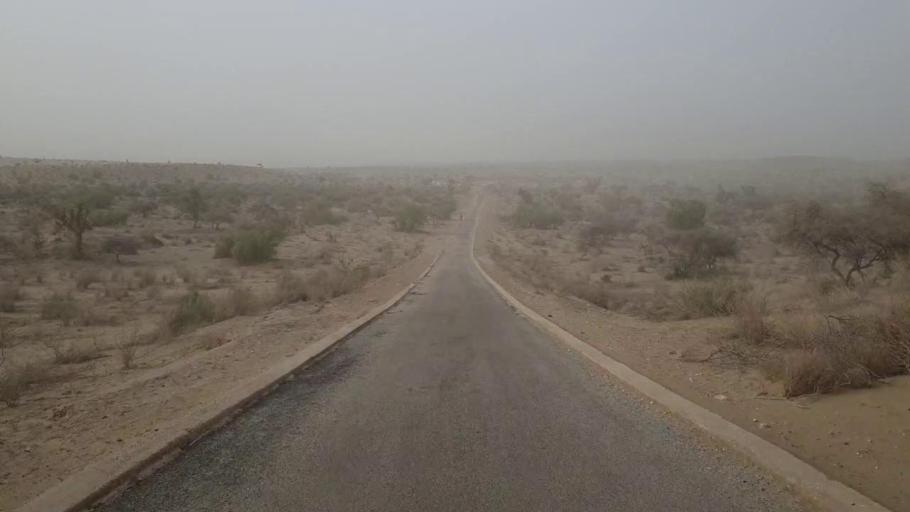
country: PK
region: Sindh
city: Islamkot
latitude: 24.5669
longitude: 70.3631
